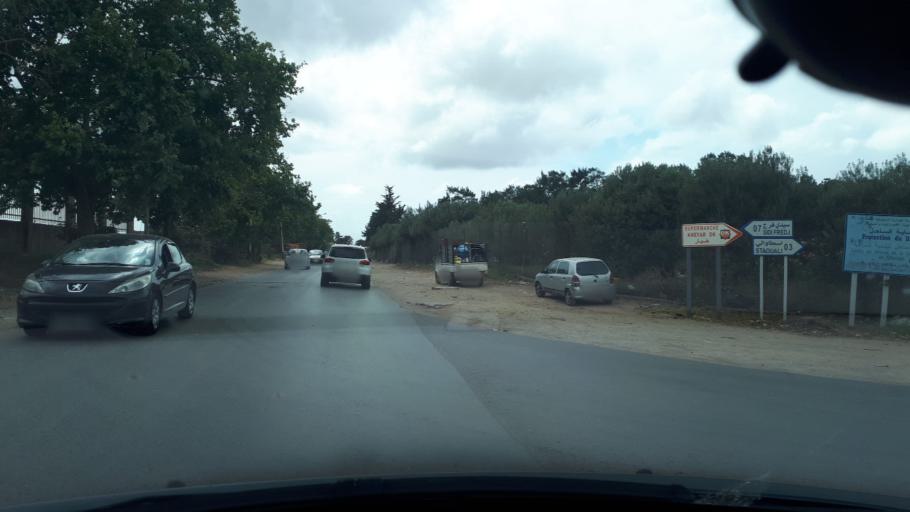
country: DZ
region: Tipaza
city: Cheraga
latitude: 36.7426
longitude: 2.9068
